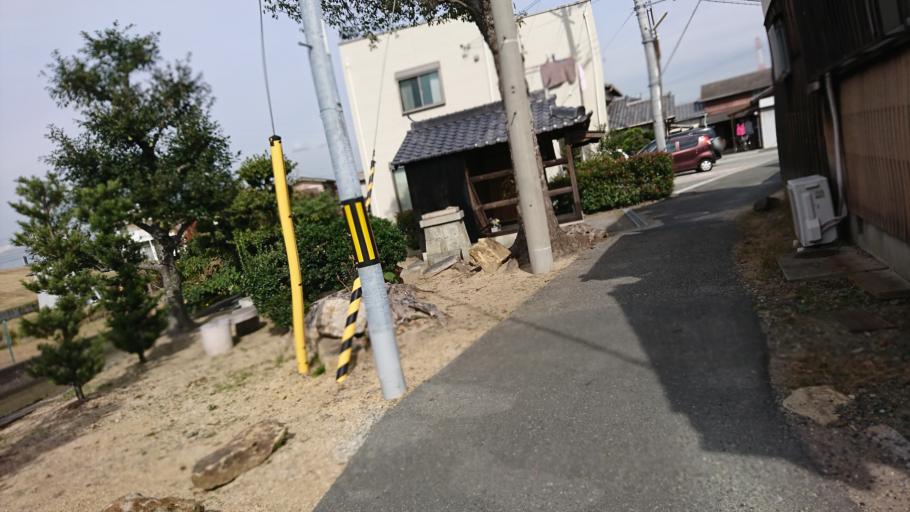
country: JP
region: Hyogo
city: Kakogawacho-honmachi
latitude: 34.7517
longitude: 134.8124
